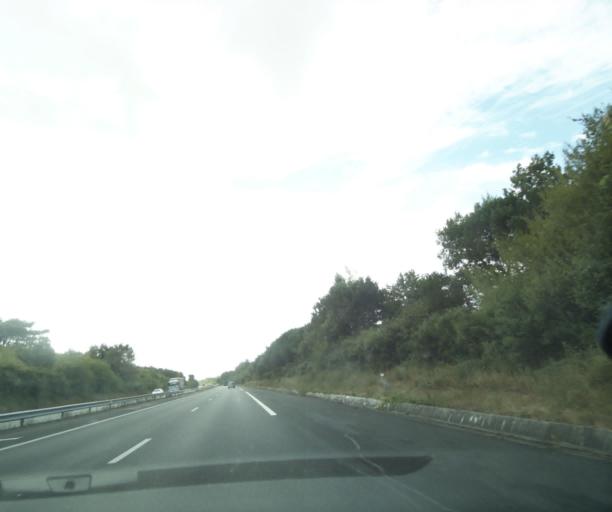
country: FR
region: Poitou-Charentes
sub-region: Departement de la Charente-Maritime
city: Thenac
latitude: 45.6521
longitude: -0.6335
